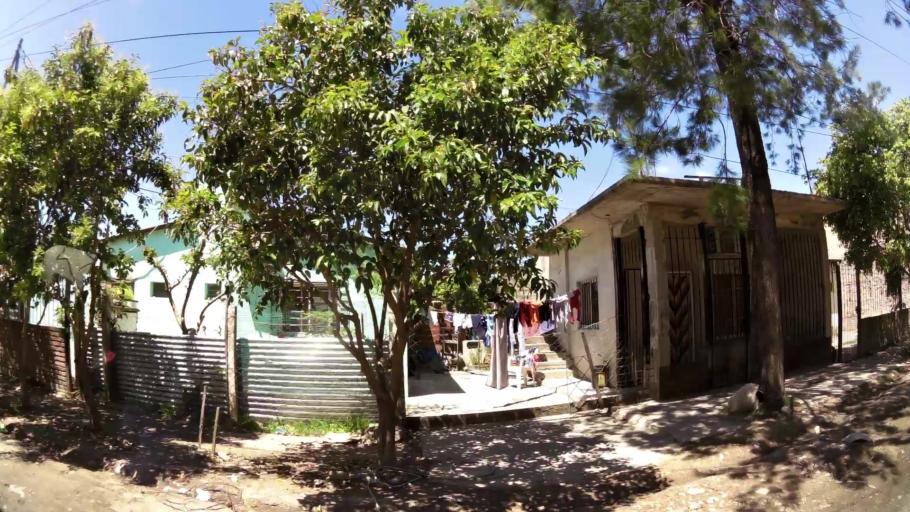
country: AR
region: Buenos Aires
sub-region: Partido de Quilmes
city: Quilmes
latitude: -34.7128
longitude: -58.3153
